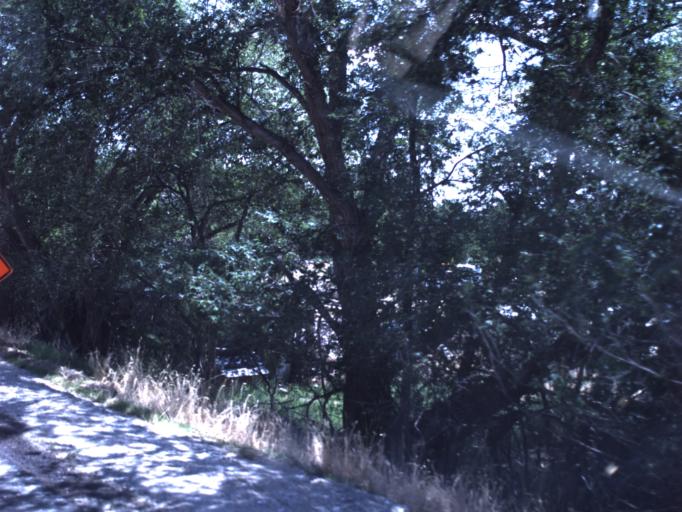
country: US
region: Utah
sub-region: Emery County
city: Orangeville
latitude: 39.2377
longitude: -111.0546
